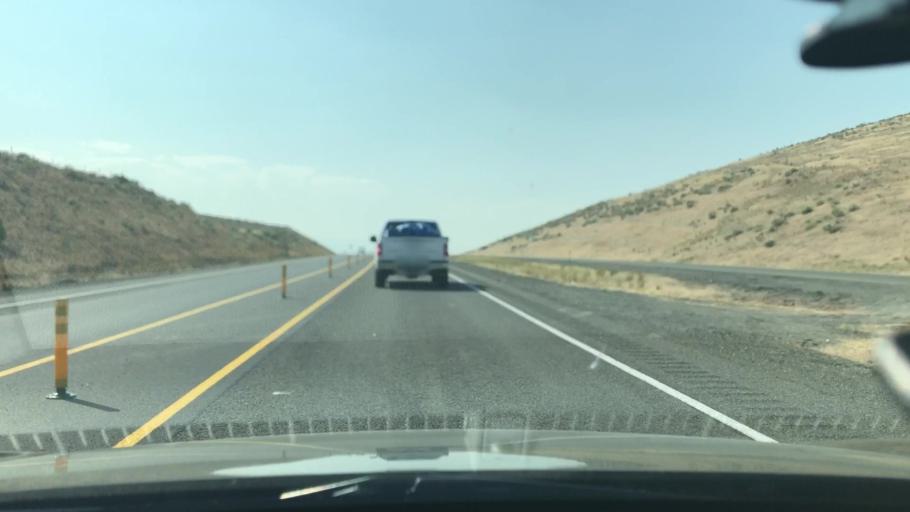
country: US
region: Oregon
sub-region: Baker County
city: Baker City
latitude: 44.6833
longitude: -117.6611
